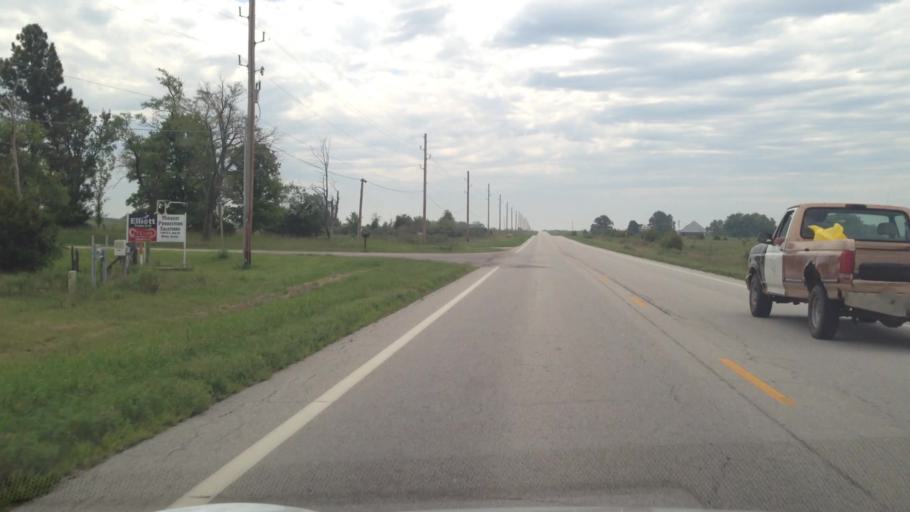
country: US
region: Kansas
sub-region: Allen County
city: Iola
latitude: 37.9460
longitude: -95.1700
